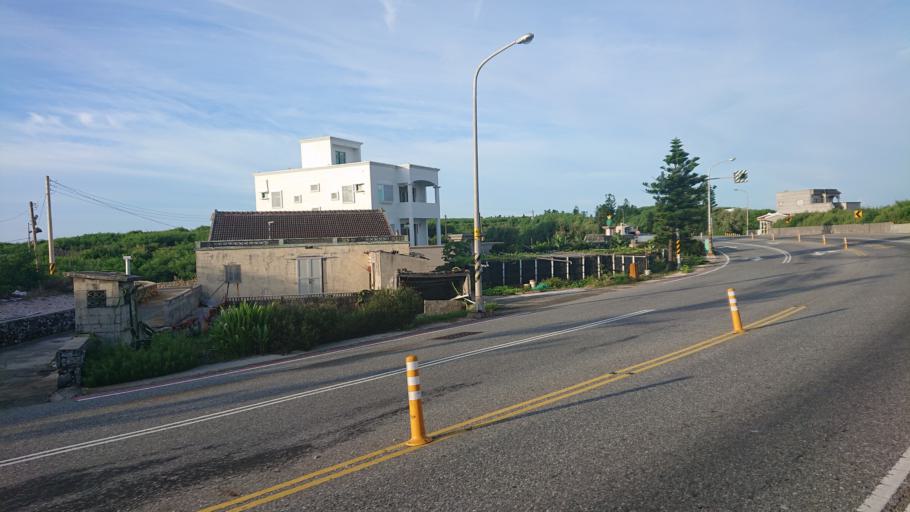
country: TW
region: Taiwan
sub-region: Penghu
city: Ma-kung
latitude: 23.6360
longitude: 119.5355
